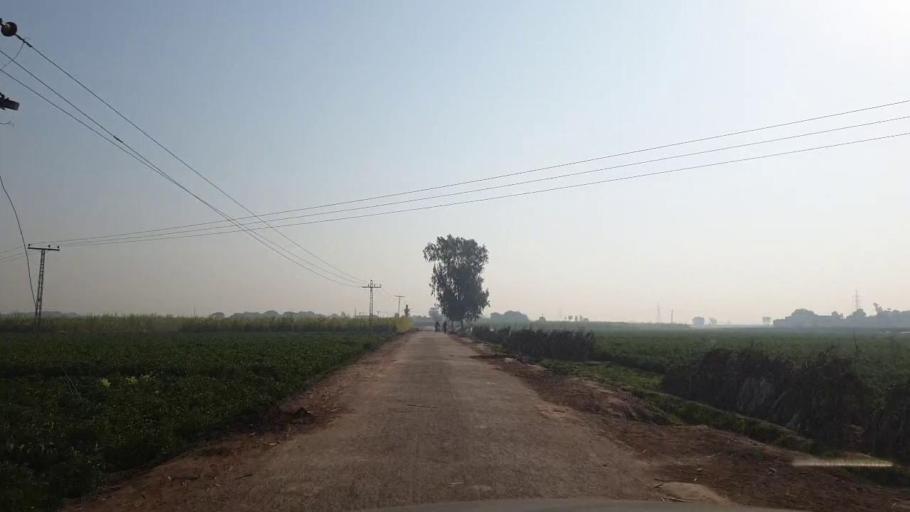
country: PK
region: Sindh
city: Tando Allahyar
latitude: 25.4919
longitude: 68.7268
